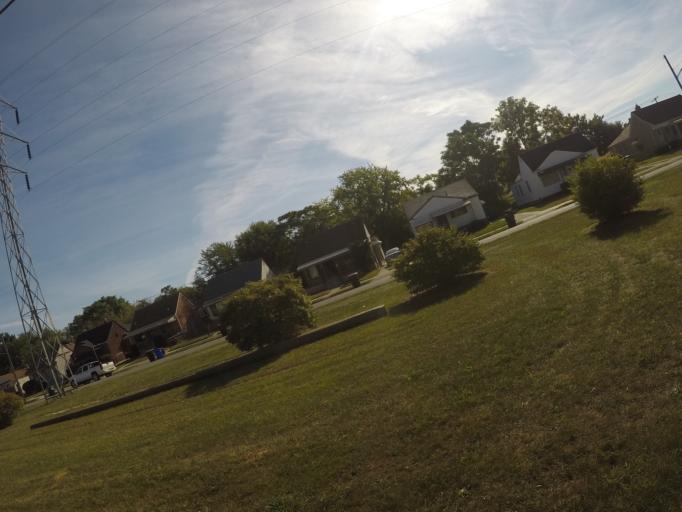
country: US
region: Michigan
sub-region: Wayne County
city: Lincoln Park
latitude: 42.2612
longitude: -83.1653
